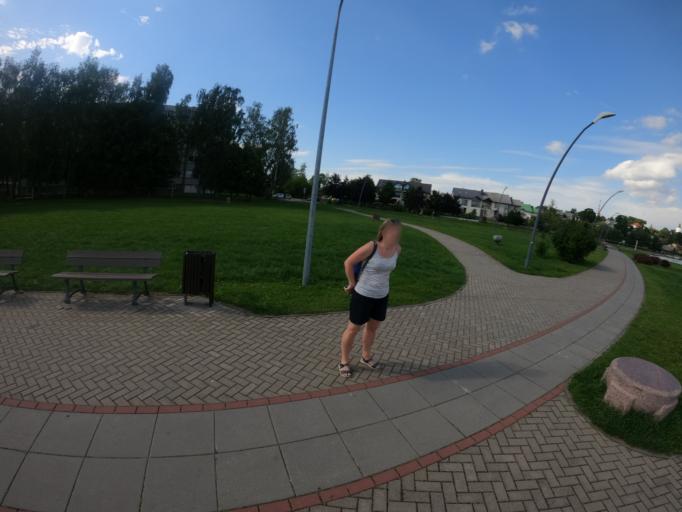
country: LT
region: Telsiu apskritis
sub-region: Telsiai
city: Telsiai
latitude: 55.9763
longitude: 22.2393
